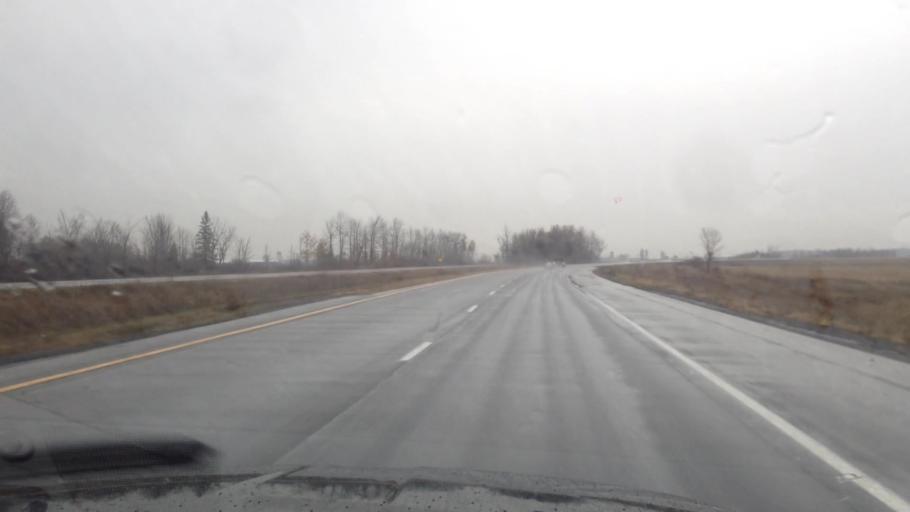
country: CA
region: Ontario
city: Casselman
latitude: 45.3548
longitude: -74.8868
